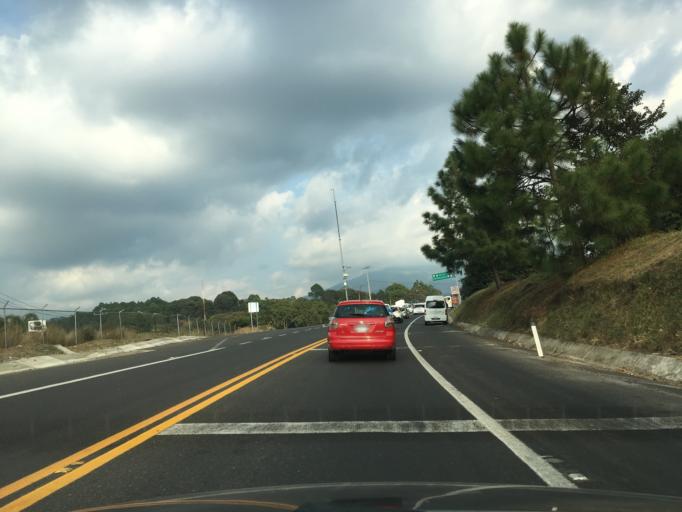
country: MX
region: Michoacan
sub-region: Ziracuaretiro
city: Patuan
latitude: 19.4405
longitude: -101.8856
